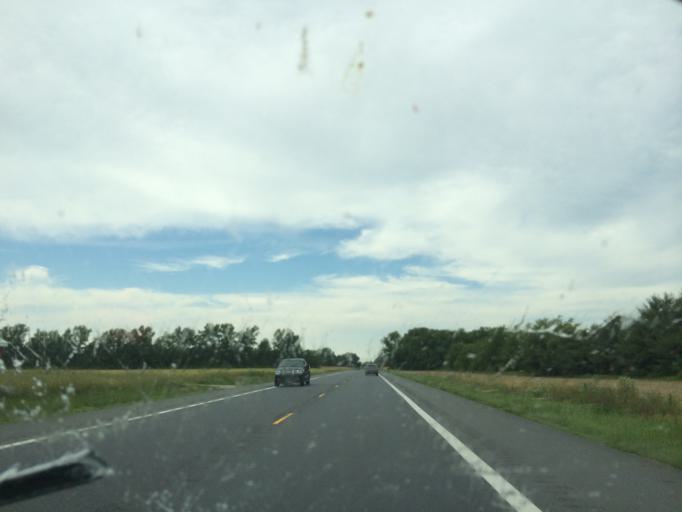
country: US
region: Maryland
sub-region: Caroline County
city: Denton
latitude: 38.8100
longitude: -75.7418
